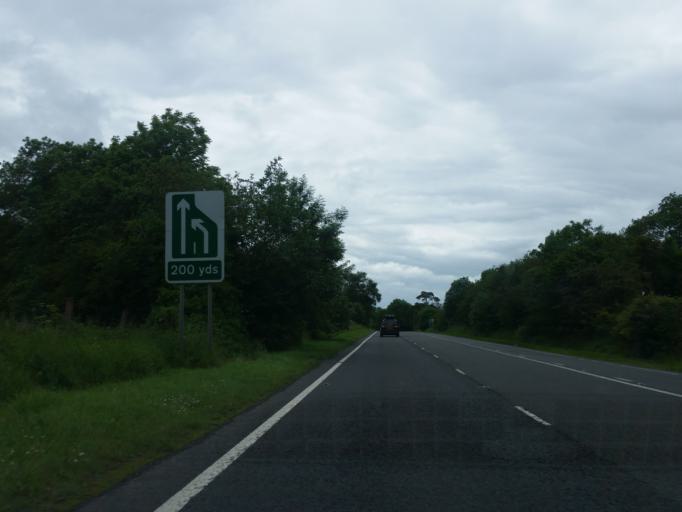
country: GB
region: Northern Ireland
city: Fivemiletown
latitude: 54.3819
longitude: -7.2785
